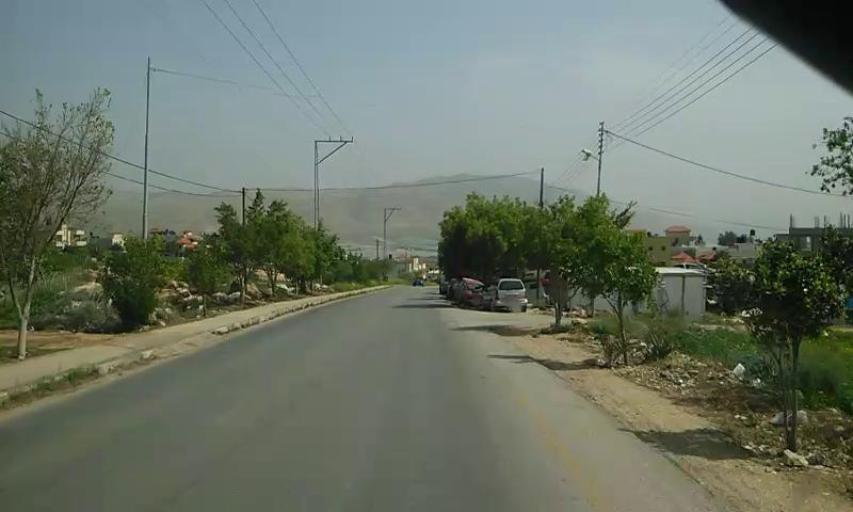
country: PS
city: Al Badhan
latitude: 32.2623
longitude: 35.3333
